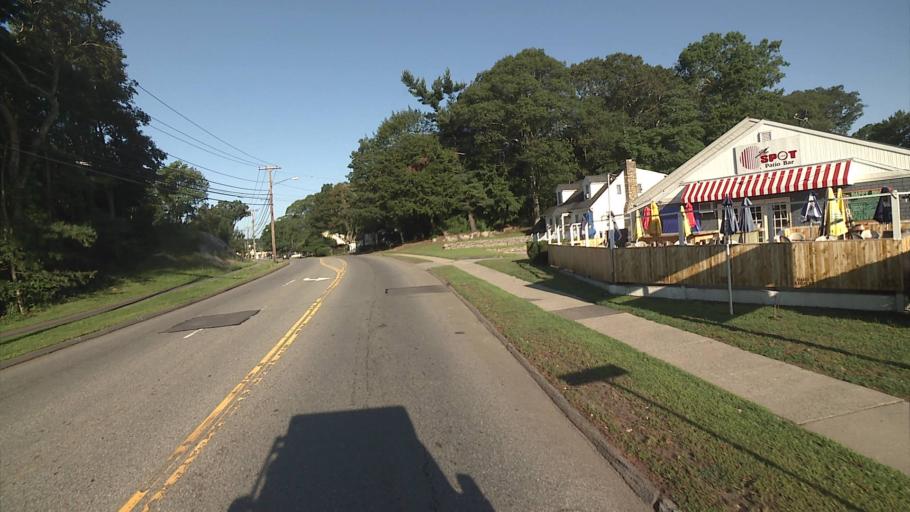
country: US
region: Connecticut
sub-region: New London County
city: Long Hill
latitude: 41.3468
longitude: -72.0436
